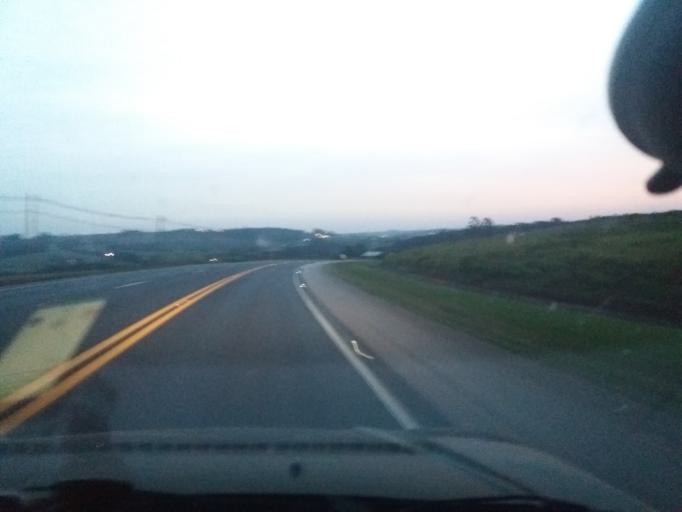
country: BR
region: Sao Paulo
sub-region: Itapeva
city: Itapeva
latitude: -23.9783
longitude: -48.8344
